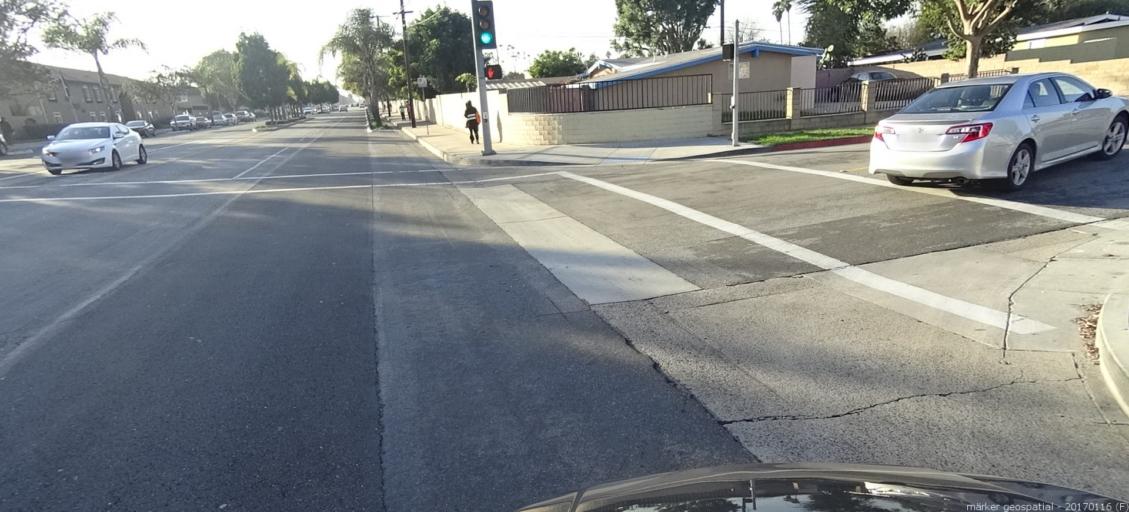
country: US
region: California
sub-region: Orange County
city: Stanton
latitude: 33.7885
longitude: -117.9874
